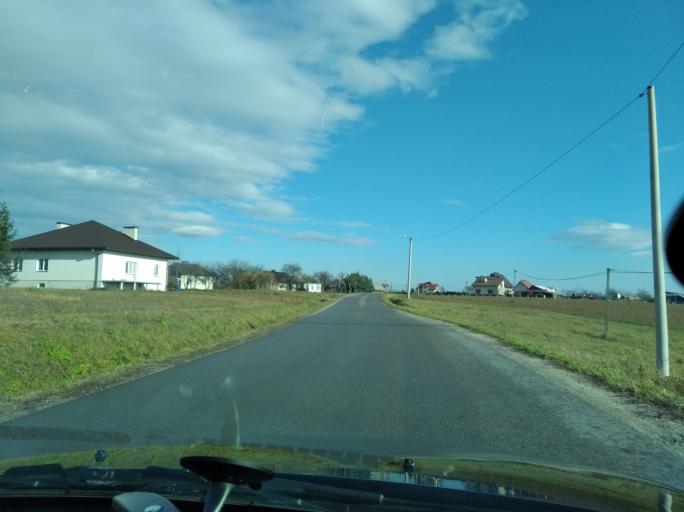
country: PL
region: Subcarpathian Voivodeship
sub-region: Powiat ropczycko-sedziszowski
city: Niedzwiada
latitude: 50.0087
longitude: 21.4756
